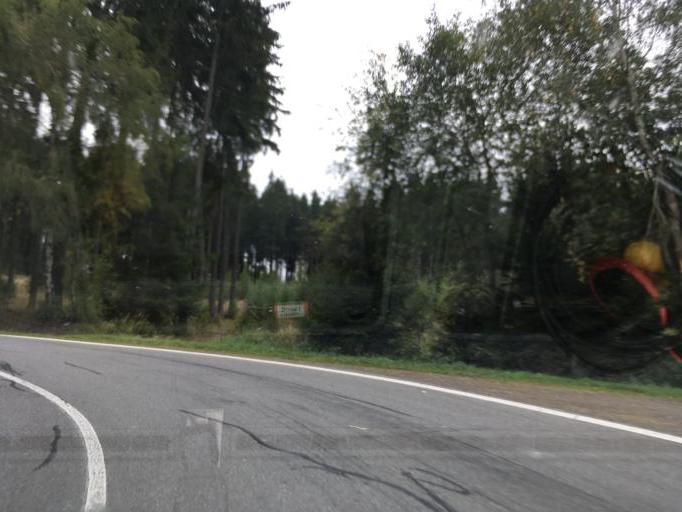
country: CZ
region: Central Bohemia
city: Cechtice
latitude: 49.5760
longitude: 15.0989
